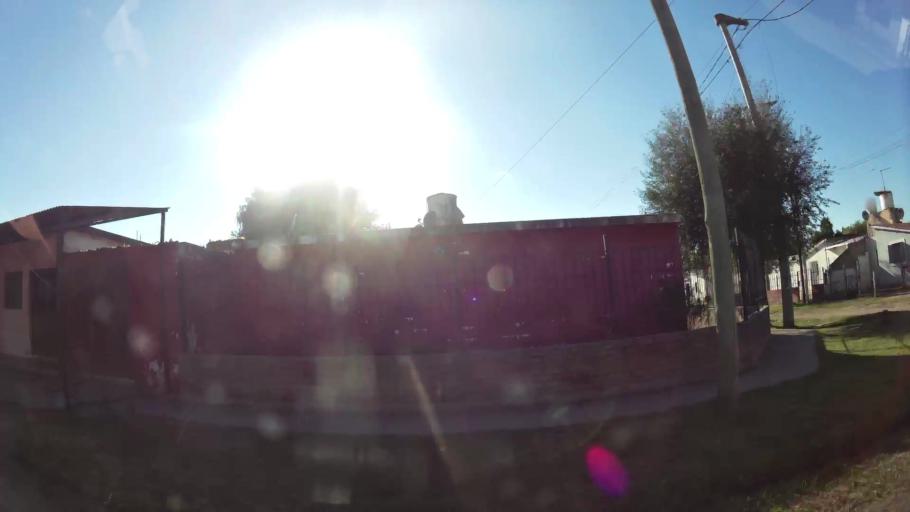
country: AR
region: Cordoba
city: Villa Allende
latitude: -31.3353
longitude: -64.2434
